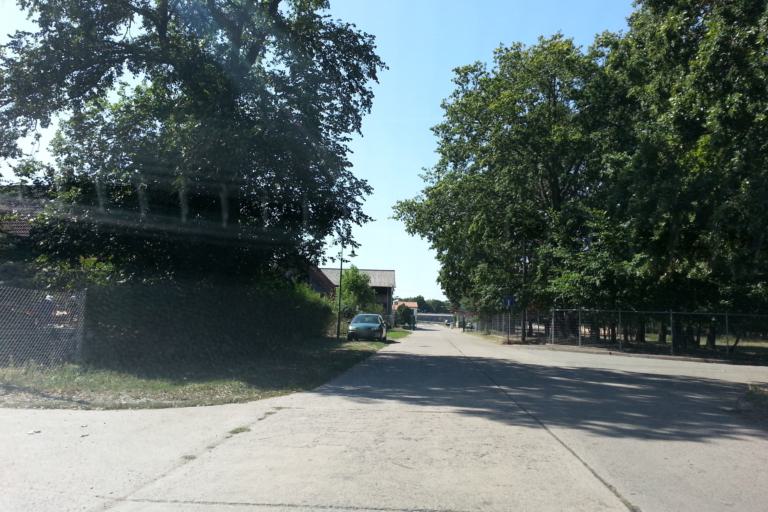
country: DE
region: Mecklenburg-Vorpommern
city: Ferdinandshof
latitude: 53.6445
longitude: 13.9120
